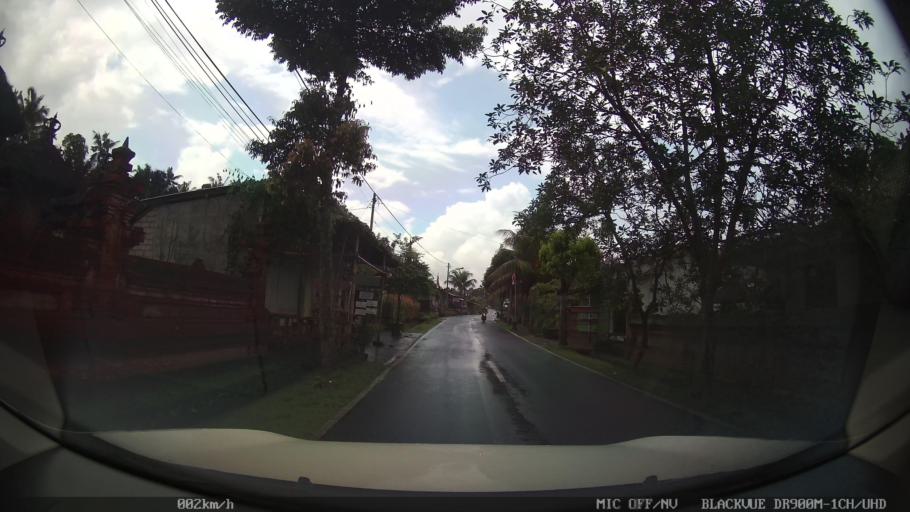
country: ID
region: Bali
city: Banjar Teguan
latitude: -8.5024
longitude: 115.2327
